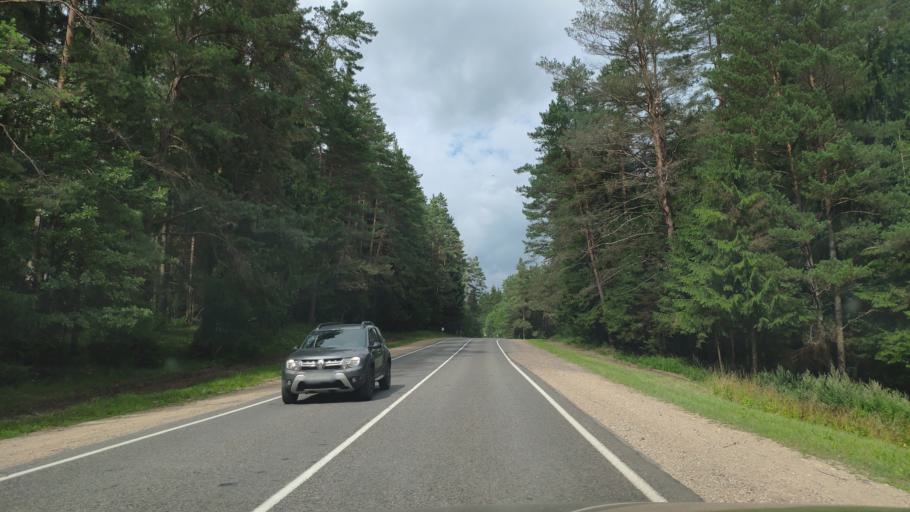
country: BY
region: Minsk
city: Zaslawye
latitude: 53.9761
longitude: 27.2491
